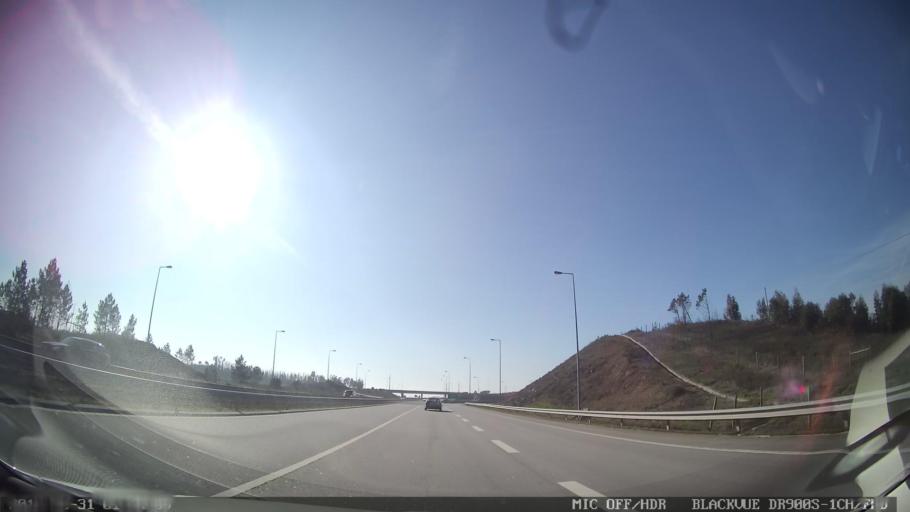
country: PT
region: Portalegre
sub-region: Nisa
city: Nisa
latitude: 39.5613
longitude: -7.7992
